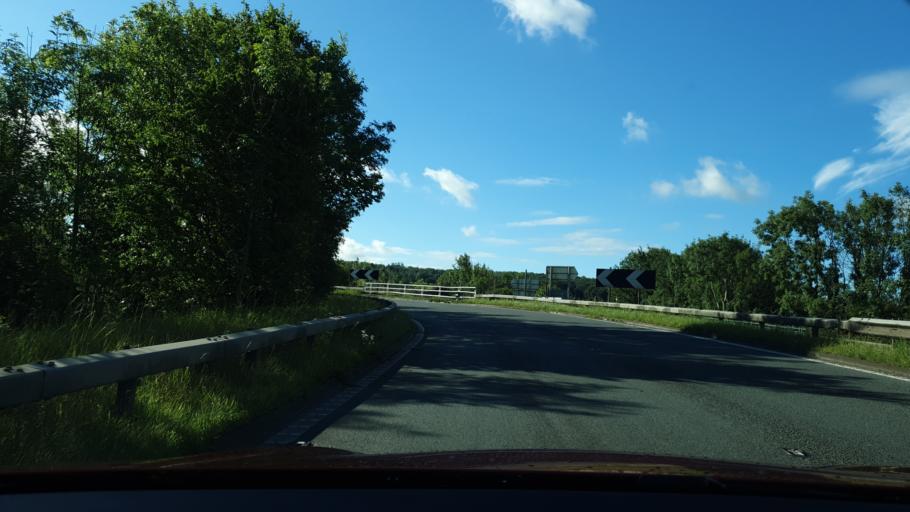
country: GB
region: England
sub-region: Lancashire
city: Carnforth
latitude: 54.1299
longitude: -2.7511
